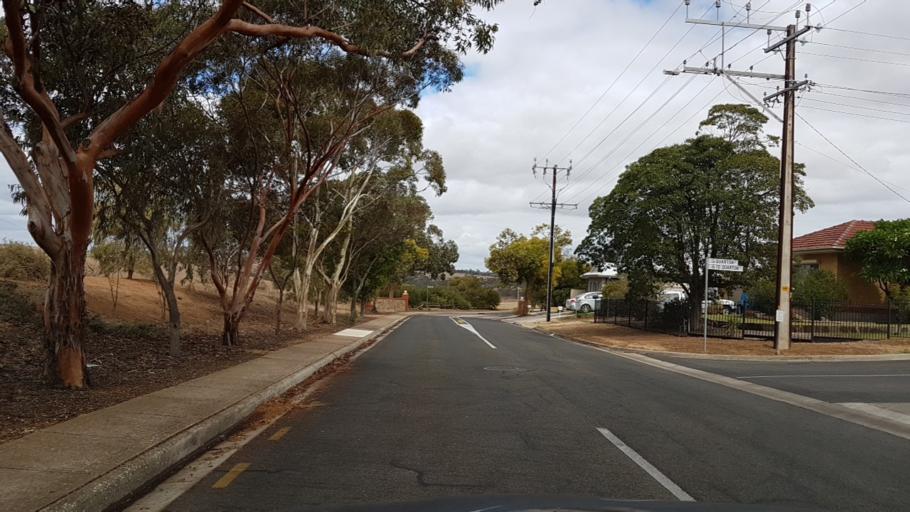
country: AU
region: South Australia
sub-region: Gawler
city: Gawler
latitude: -34.6041
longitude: 138.7633
